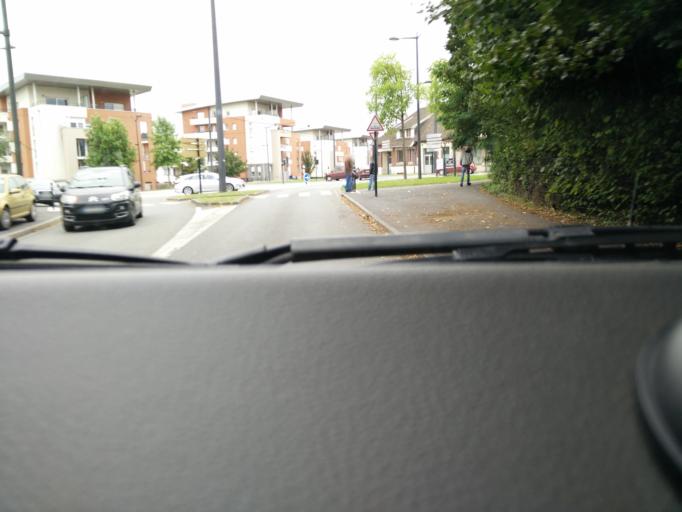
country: FR
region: Nord-Pas-de-Calais
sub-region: Departement du Nord
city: Valenciennes
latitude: 50.3549
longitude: 3.5168
